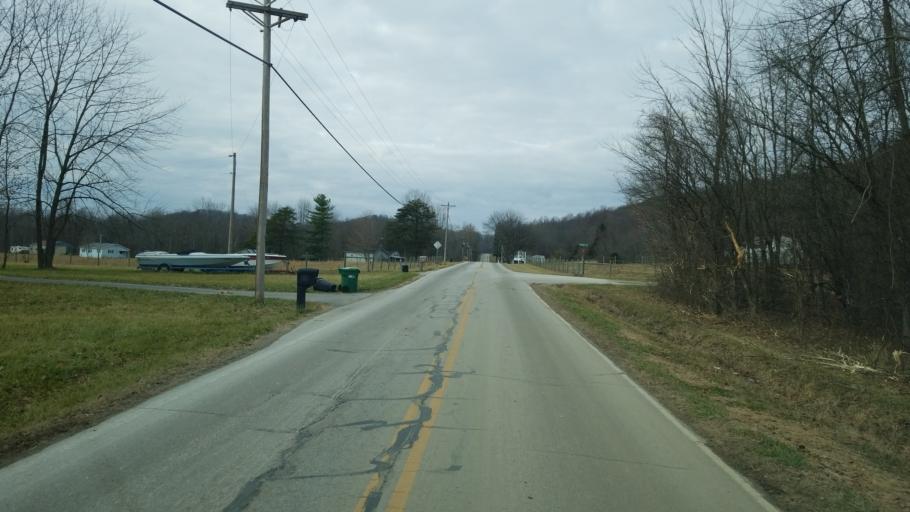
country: US
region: Ohio
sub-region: Highland County
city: Greenfield
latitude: 39.1851
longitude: -83.3567
